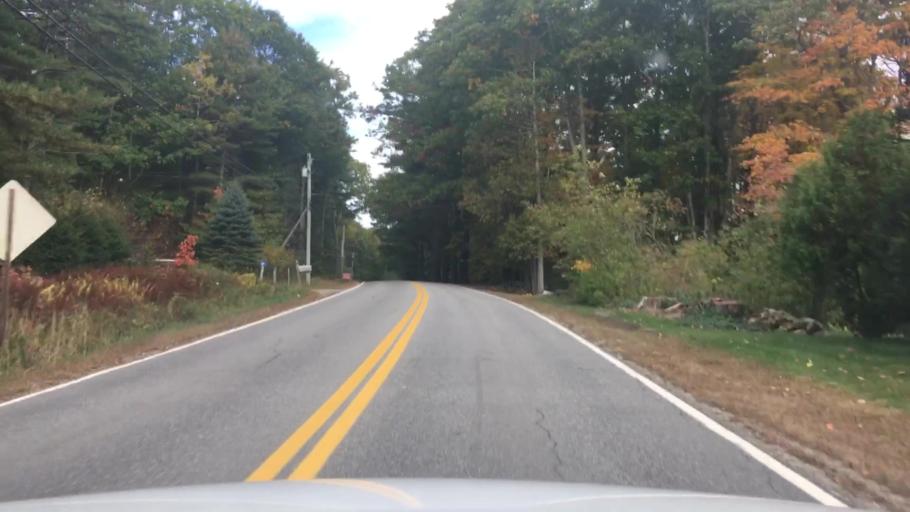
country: US
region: Maine
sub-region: Knox County
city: Hope
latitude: 44.2649
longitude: -69.1343
